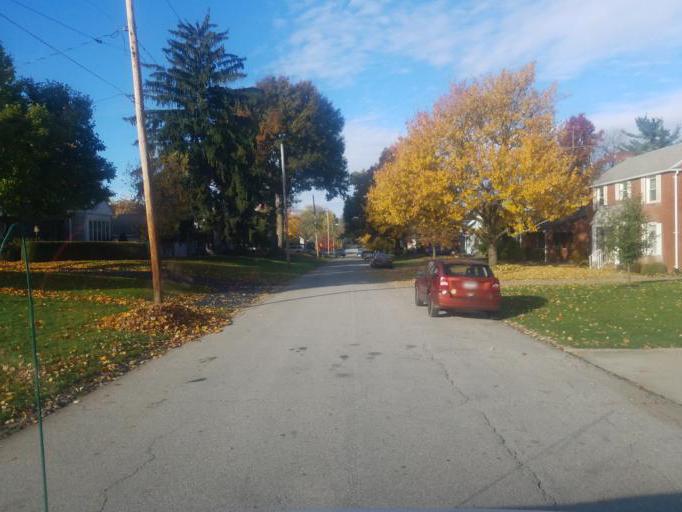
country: US
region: Ohio
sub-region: Richland County
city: Mansfield
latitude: 40.7491
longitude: -82.5387
